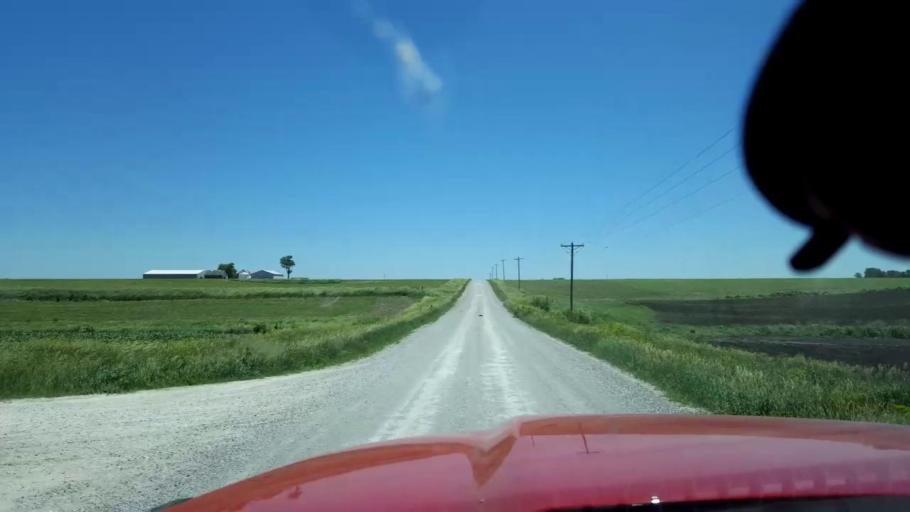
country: US
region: Iowa
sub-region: Washington County
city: Washington
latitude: 41.2793
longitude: -91.6508
